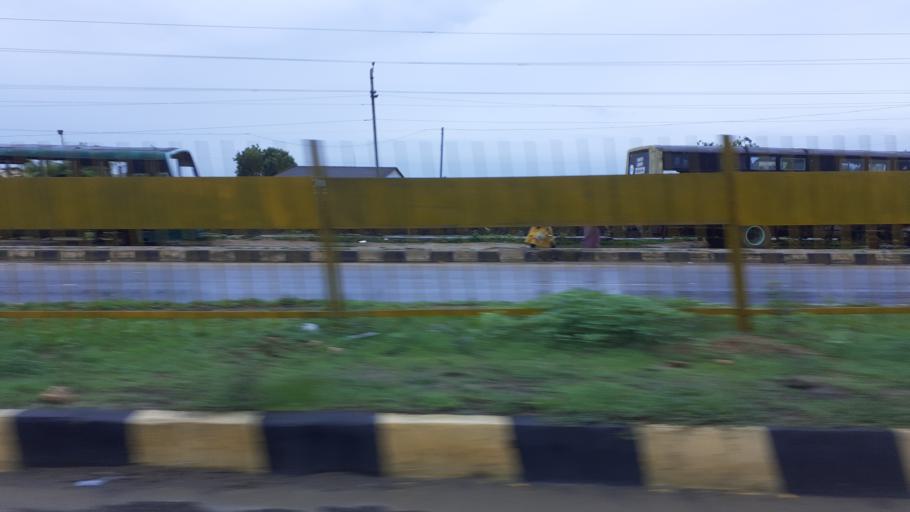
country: IN
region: Tamil Nadu
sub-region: Tirunelveli Kattabo
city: Tirunelveli
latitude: 8.7138
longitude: 77.7725
